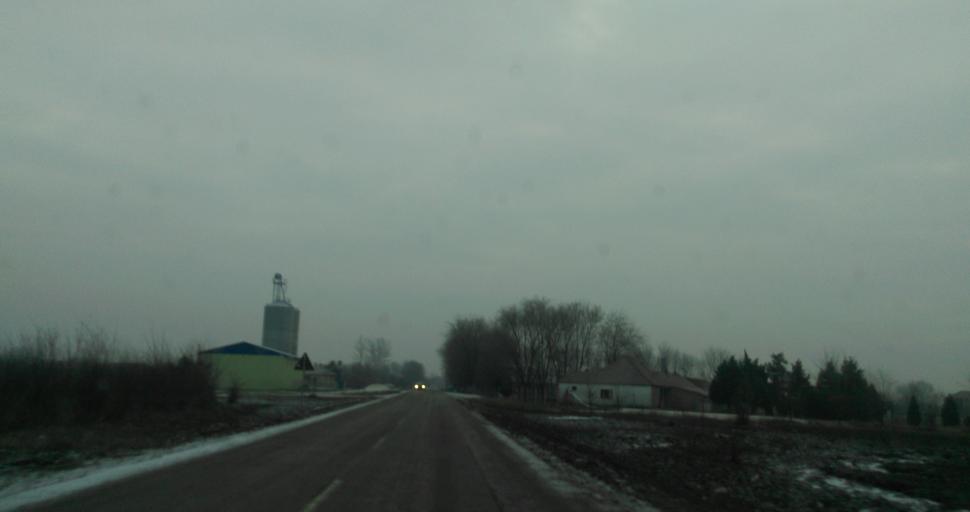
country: RS
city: Kumane
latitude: 45.5376
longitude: 20.2135
